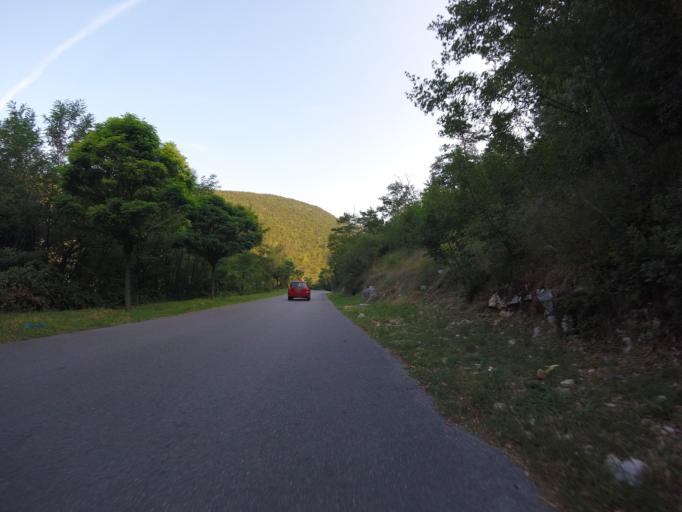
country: HR
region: Primorsko-Goranska
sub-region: Grad Crikvenica
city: Crikvenica
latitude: 45.1823
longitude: 14.6971
